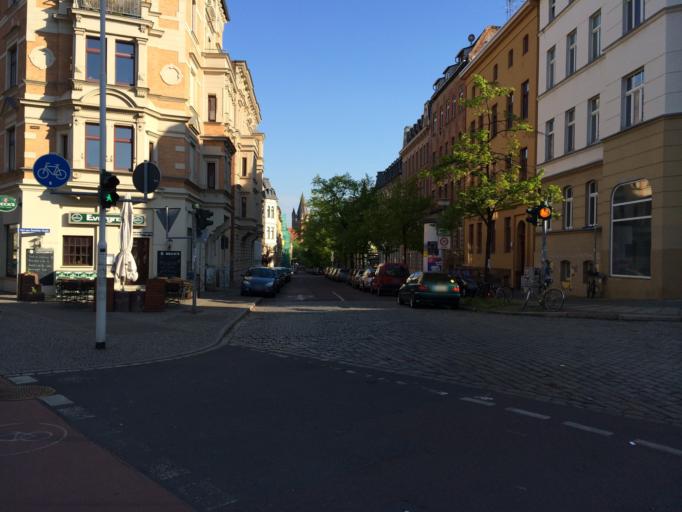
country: DE
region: Saxony-Anhalt
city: Halle (Saale)
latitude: 51.4910
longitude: 11.9755
